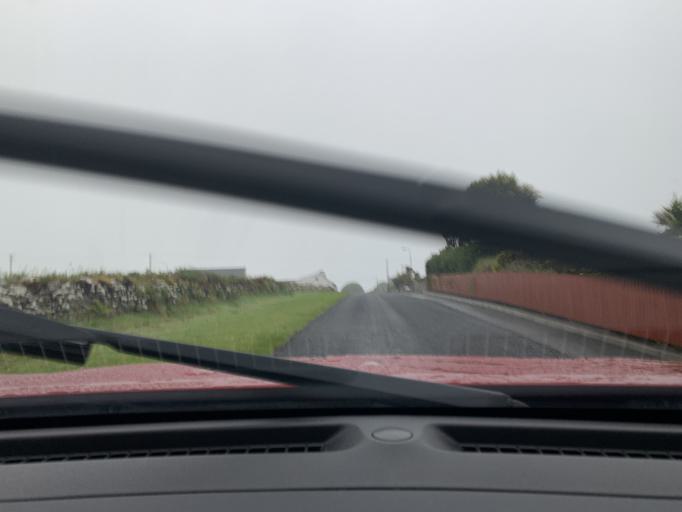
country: IE
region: Ulster
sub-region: County Donegal
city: Killybegs
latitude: 54.4681
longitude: -8.4529
